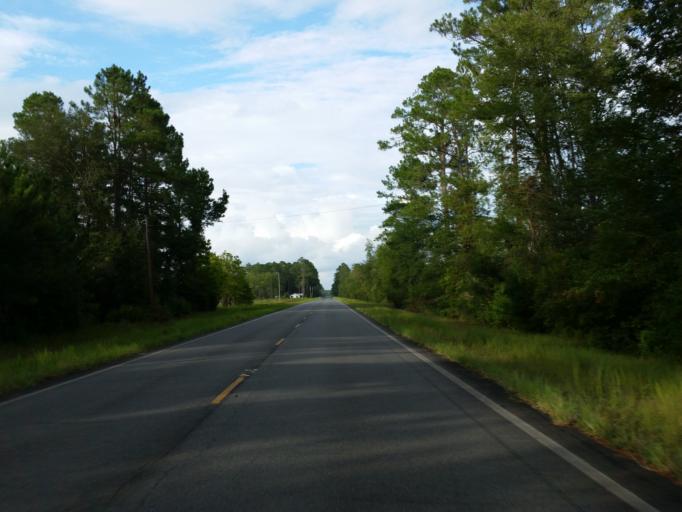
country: US
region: Florida
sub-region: Hamilton County
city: Jasper
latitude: 30.6419
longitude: -82.5774
